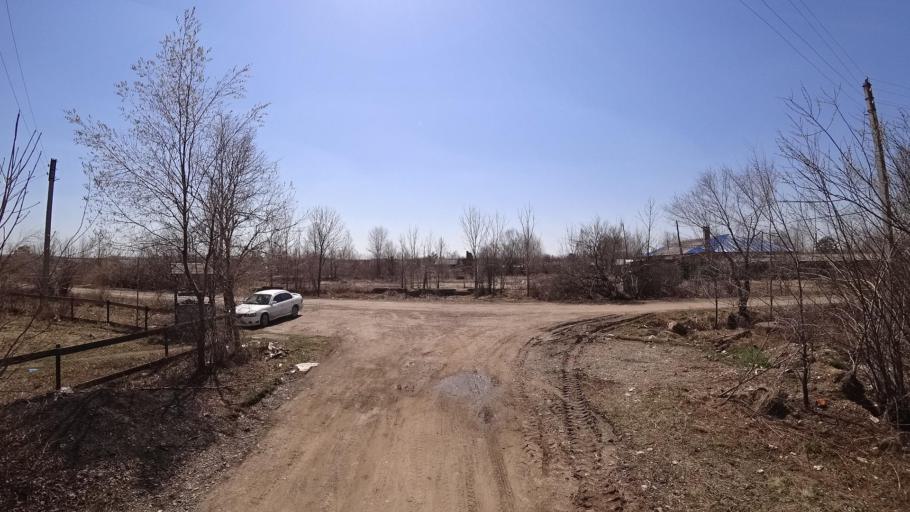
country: RU
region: Khabarovsk Krai
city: Khurba
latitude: 50.4053
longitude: 136.8818
